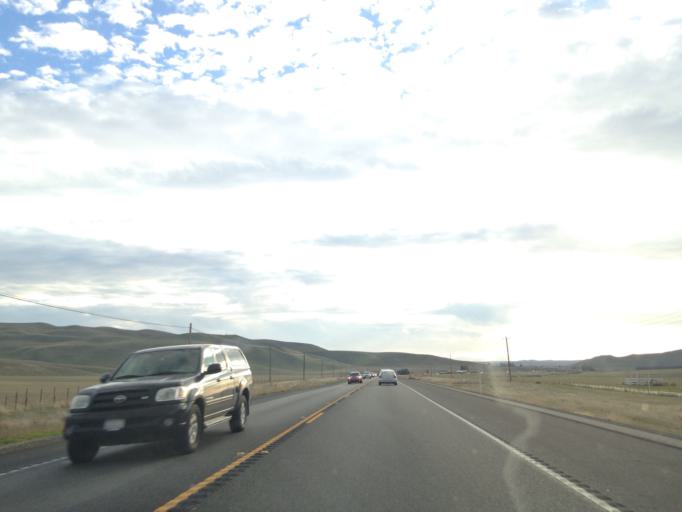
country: US
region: California
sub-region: San Luis Obispo County
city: Shandon
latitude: 35.6849
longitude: -120.3382
